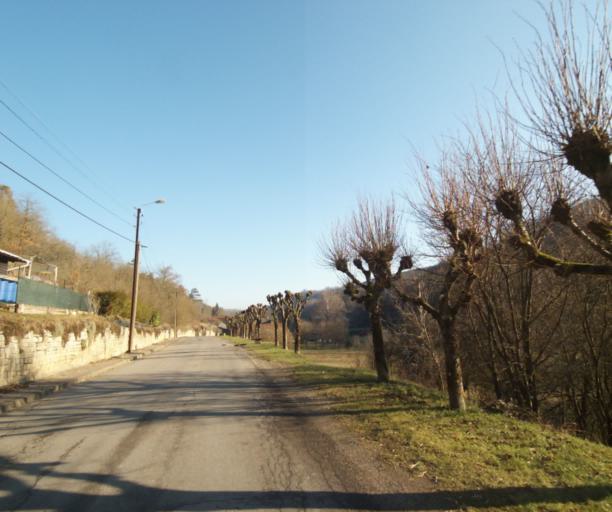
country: FR
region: Champagne-Ardenne
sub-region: Departement de la Haute-Marne
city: Chevillon
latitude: 48.5284
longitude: 5.1392
